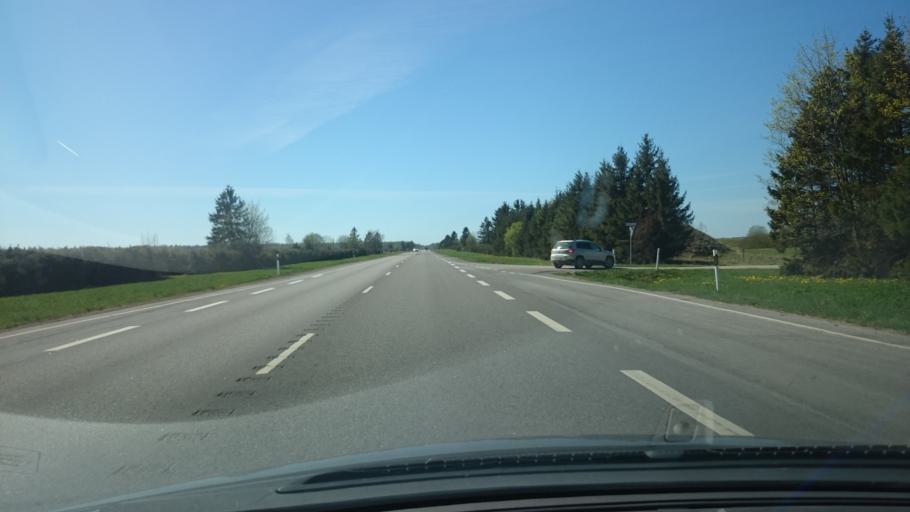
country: EE
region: Ida-Virumaa
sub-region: Sillamaee linn
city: Sillamae
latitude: 59.3919
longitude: 27.6916
